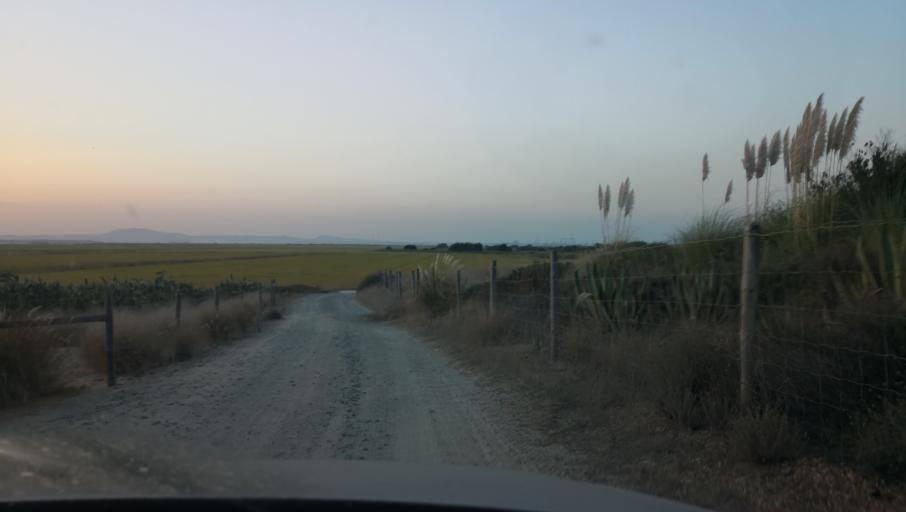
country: PT
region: Setubal
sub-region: Setubal
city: Setubal
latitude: 38.4039
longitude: -8.7736
